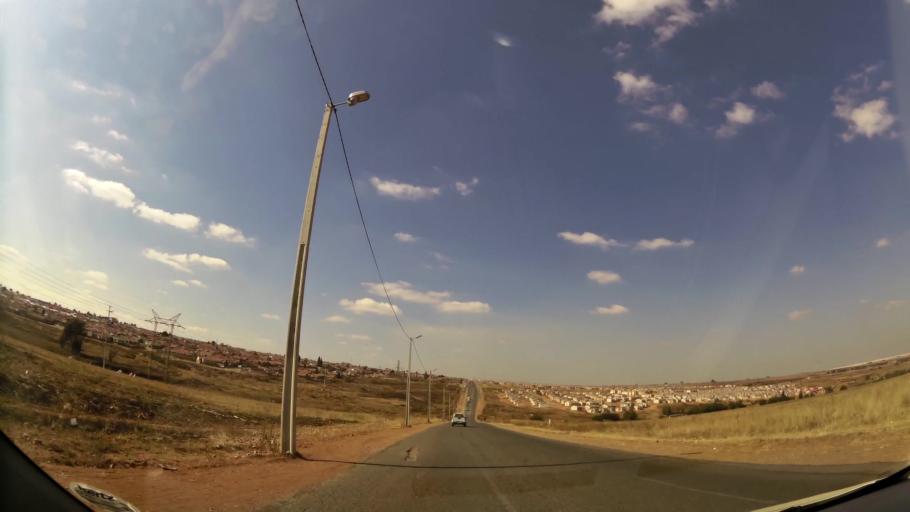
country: ZA
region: Gauteng
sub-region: West Rand District Municipality
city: Randfontein
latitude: -26.1641
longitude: 27.7648
